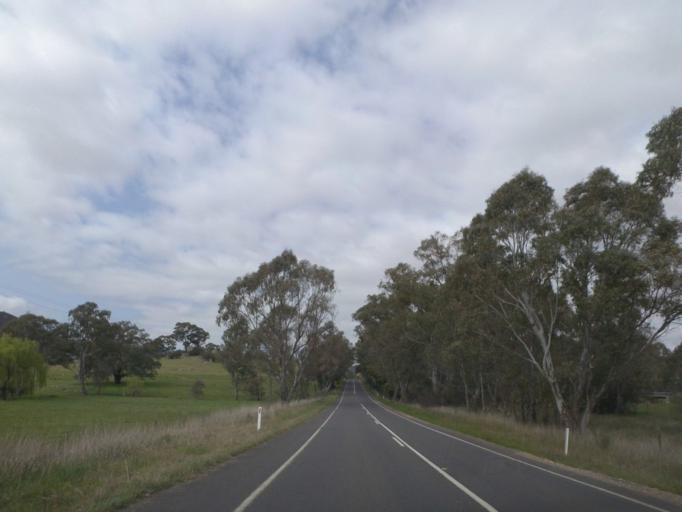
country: AU
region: Victoria
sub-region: Murrindindi
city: Kinglake West
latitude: -37.1306
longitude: 145.2273
